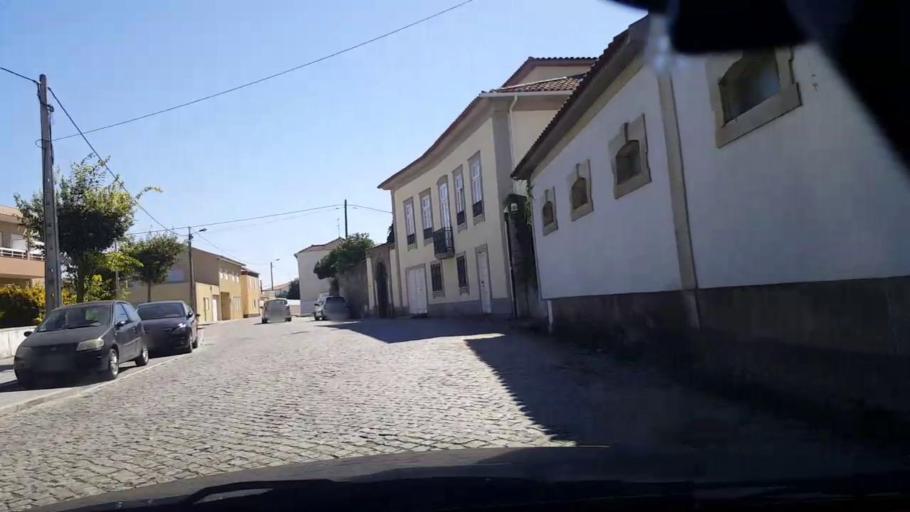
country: PT
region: Porto
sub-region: Vila do Conde
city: Arvore
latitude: 41.3157
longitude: -8.7218
